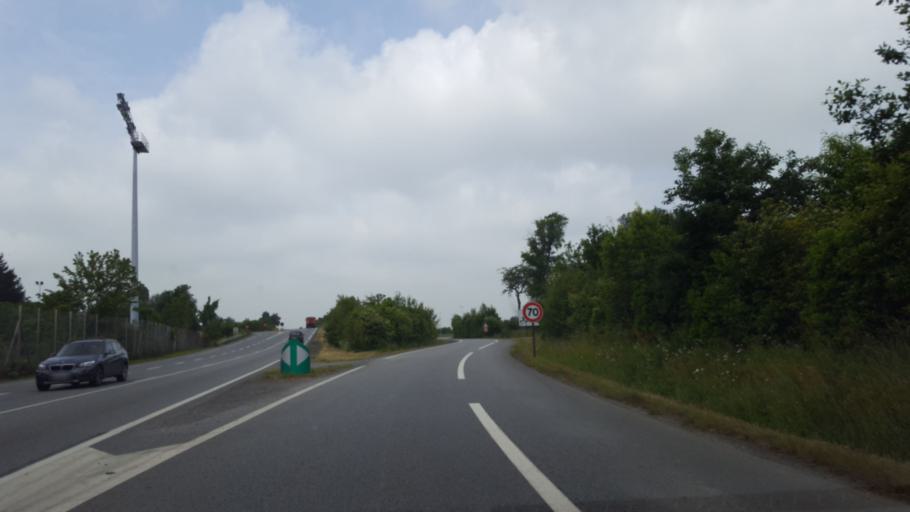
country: FR
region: Brittany
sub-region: Departement d'Ille-et-Vilaine
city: Chartres-de-Bretagne
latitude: 48.0474
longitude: -1.7047
